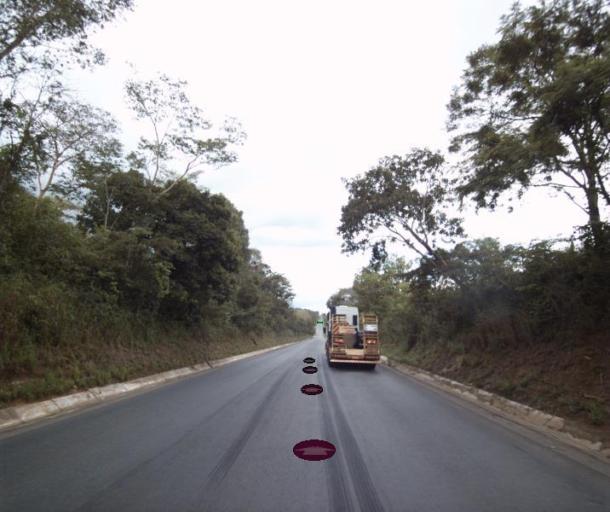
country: BR
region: Goias
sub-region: Itapaci
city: Itapaci
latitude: -15.0049
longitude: -49.4142
